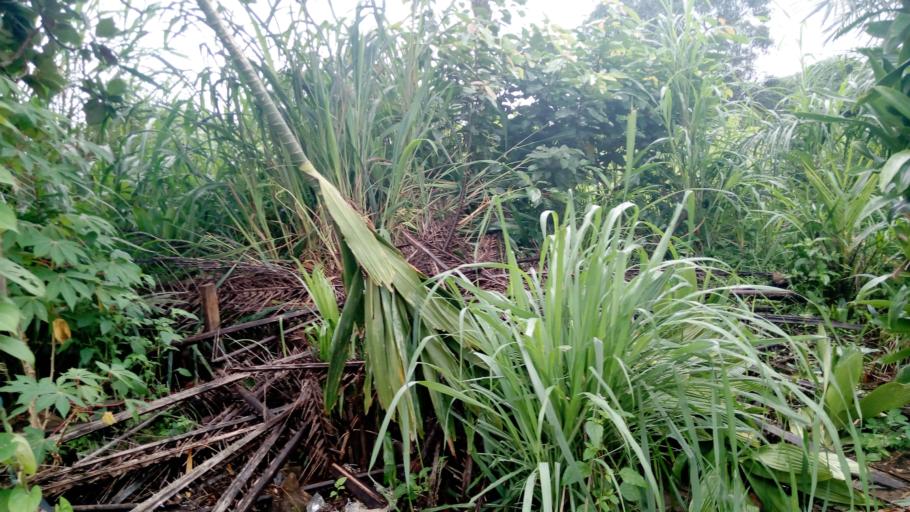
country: SL
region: Western Area
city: Waterloo
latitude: 8.3389
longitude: -12.9924
